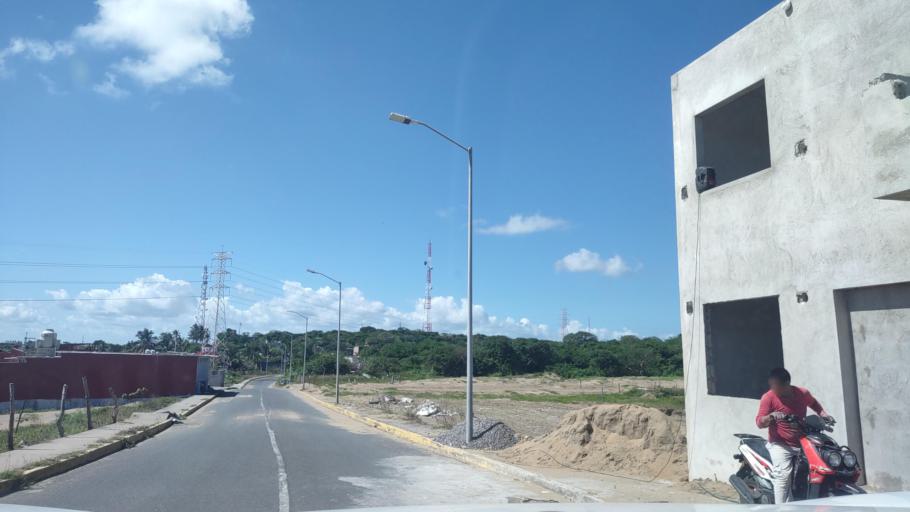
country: MX
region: Veracruz
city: Heroica Alvarado
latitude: 18.7784
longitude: -95.7617
